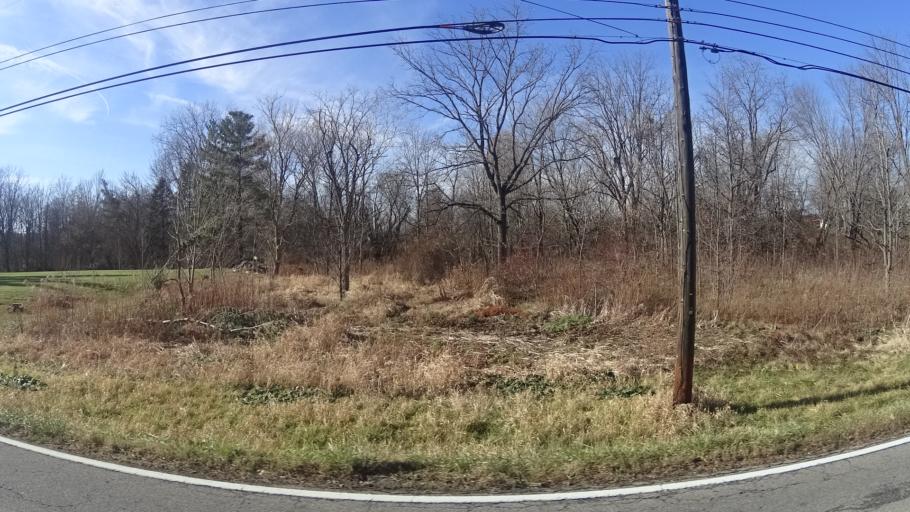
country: US
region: Ohio
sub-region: Lorain County
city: Eaton Estates
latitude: 41.3299
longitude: -82.0506
